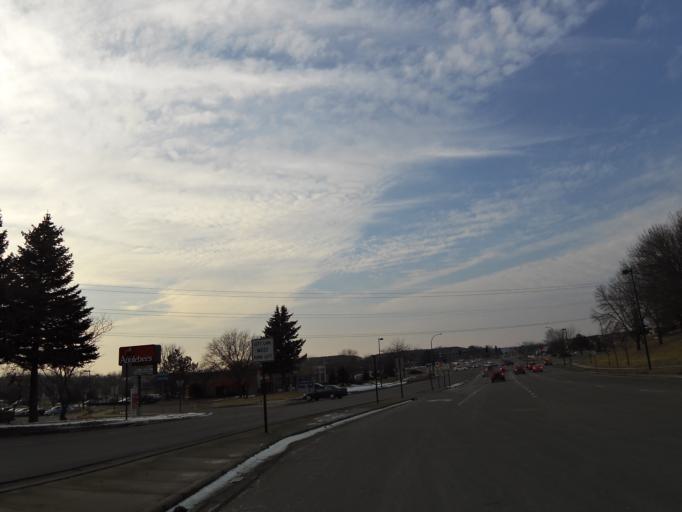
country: US
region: Minnesota
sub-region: Hennepin County
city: Eden Prairie
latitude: 44.8514
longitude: -93.4299
